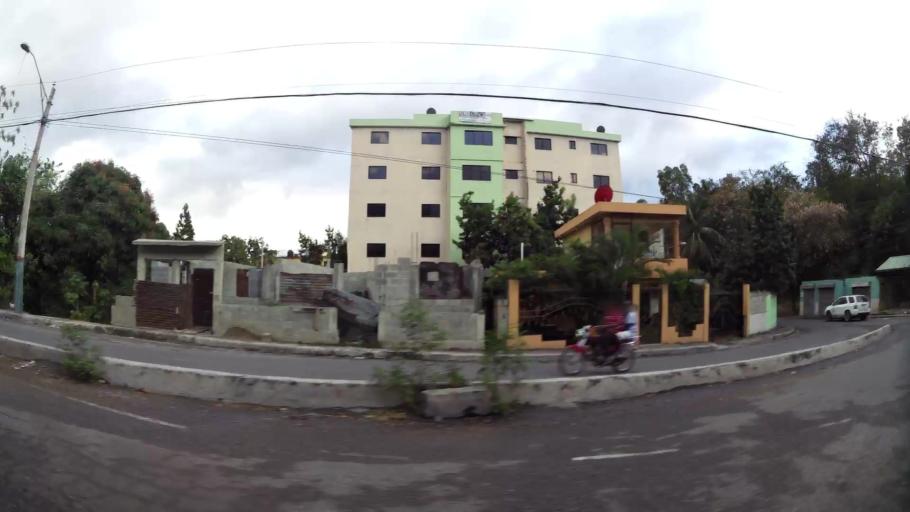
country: DO
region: Santo Domingo
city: Santo Domingo Oeste
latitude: 18.5049
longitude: -69.9987
